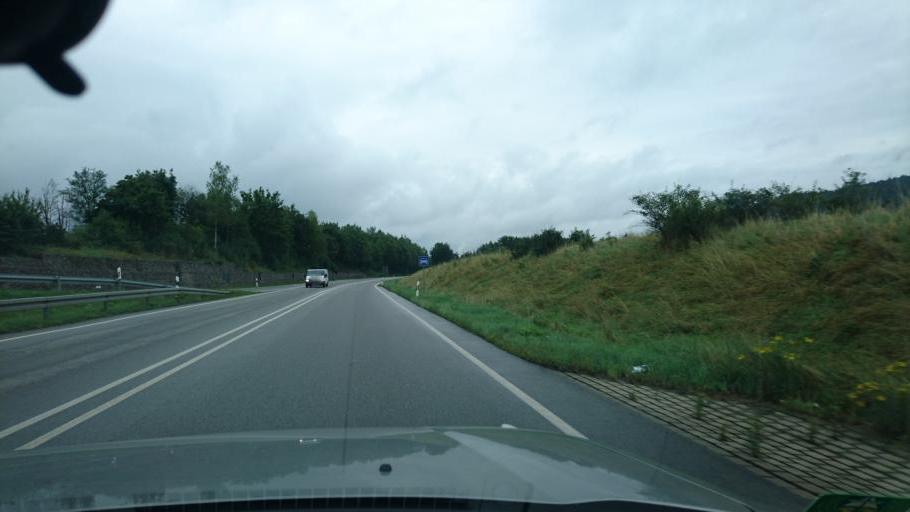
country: DE
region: Baden-Wuerttemberg
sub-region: Freiburg Region
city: Deisslingen
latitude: 48.1047
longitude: 8.6032
